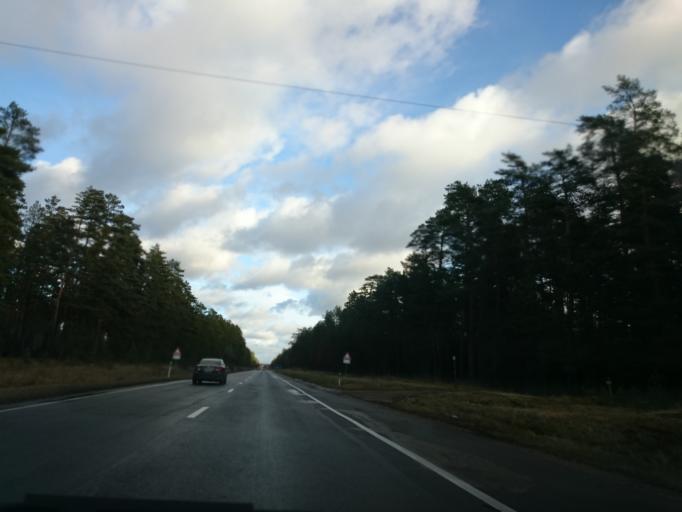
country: LV
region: Incukalns
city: Vangazi
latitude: 57.0762
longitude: 24.5126
